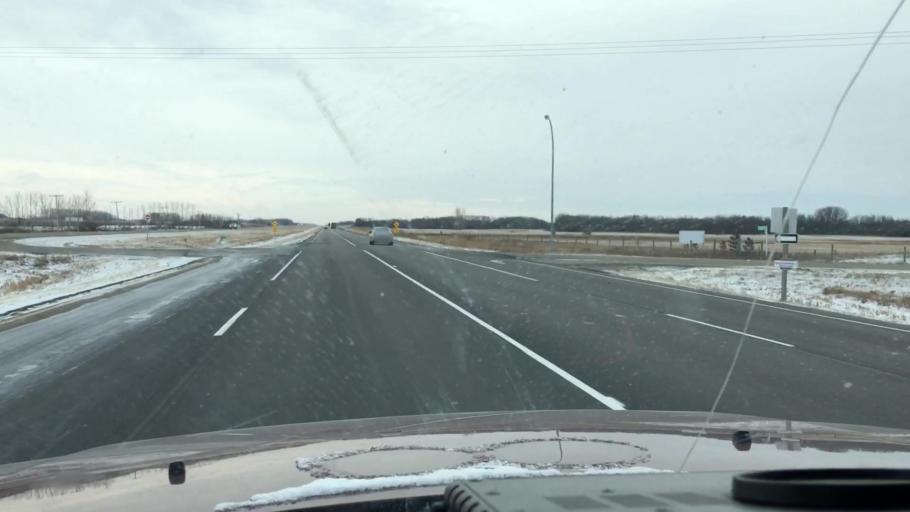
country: CA
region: Saskatchewan
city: Saskatoon
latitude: 51.9985
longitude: -106.5673
